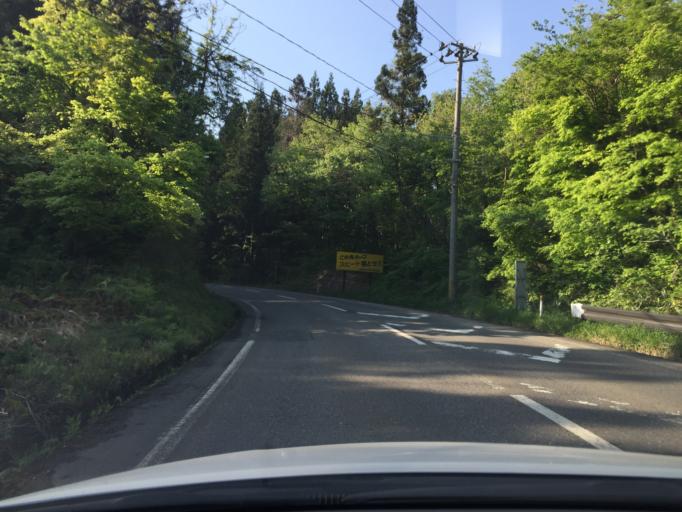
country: JP
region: Fukushima
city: Kitakata
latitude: 37.6731
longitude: 139.7823
